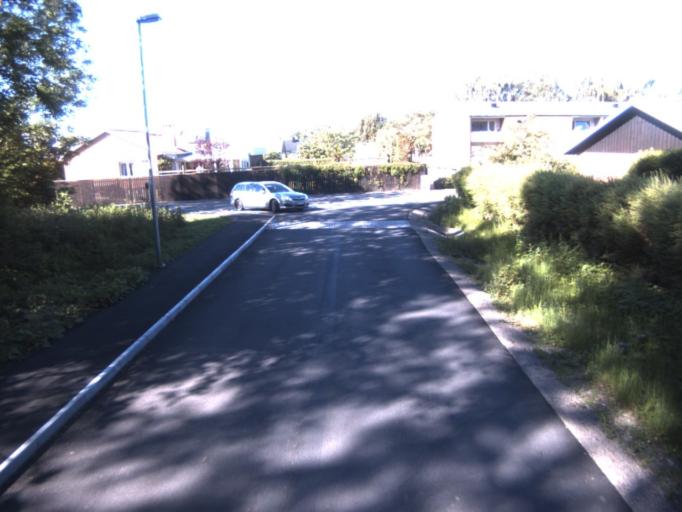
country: SE
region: Skane
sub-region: Helsingborg
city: Odakra
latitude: 56.1008
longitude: 12.7441
